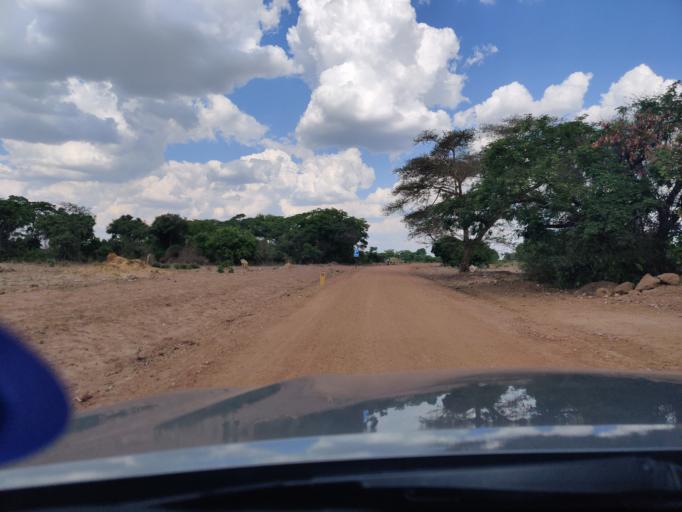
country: ZM
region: Central
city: Chibombo
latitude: -14.7614
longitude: 27.8955
